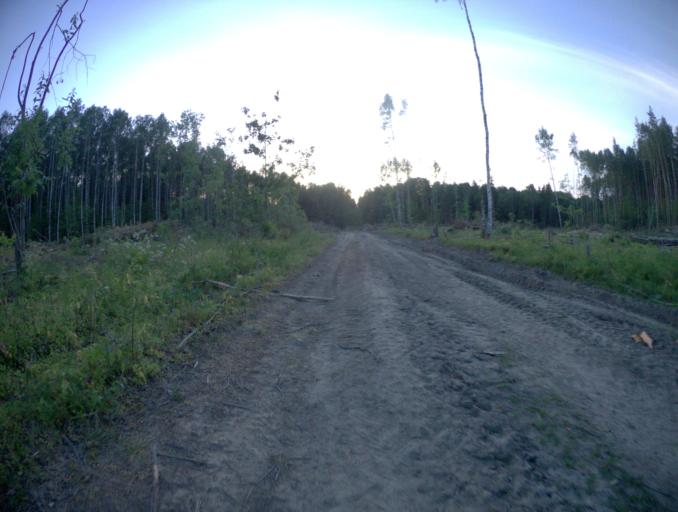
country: RU
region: Vladimir
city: Golovino
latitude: 56.0039
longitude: 40.4943
